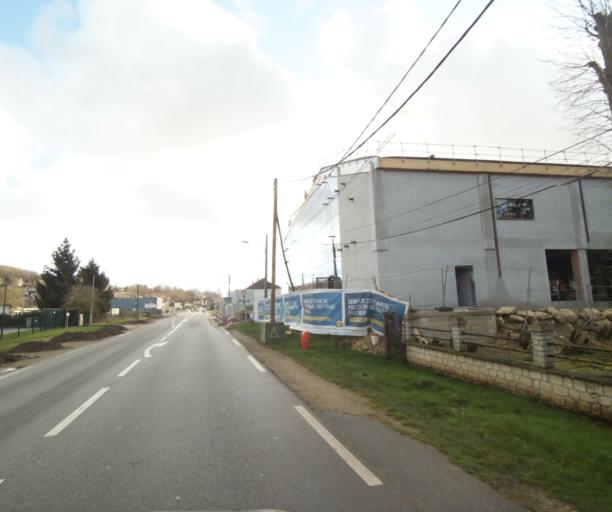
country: FR
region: Ile-de-France
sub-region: Departement des Yvelines
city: Meulan-en-Yvelines
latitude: 49.0121
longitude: 1.9021
